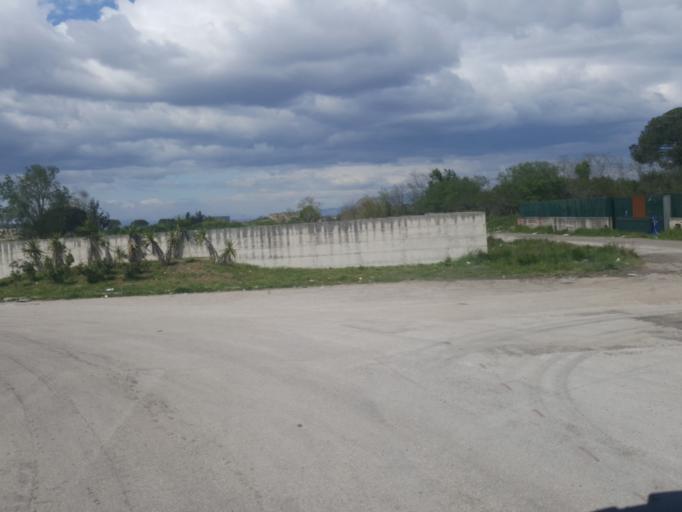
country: IT
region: Campania
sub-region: Provincia di Napoli
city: Torretta-Scalzapecora
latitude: 40.9339
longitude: 14.1226
